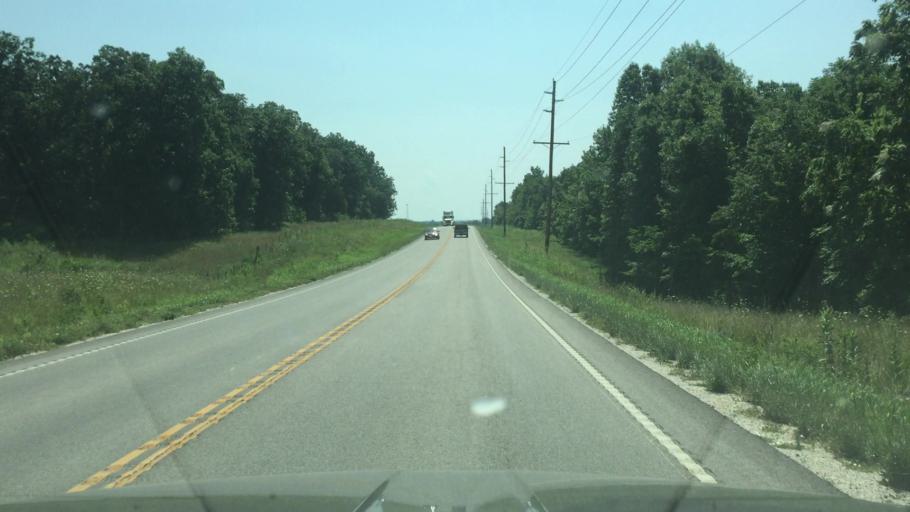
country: US
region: Missouri
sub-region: Miller County
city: Eldon
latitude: 38.3878
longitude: -92.6967
